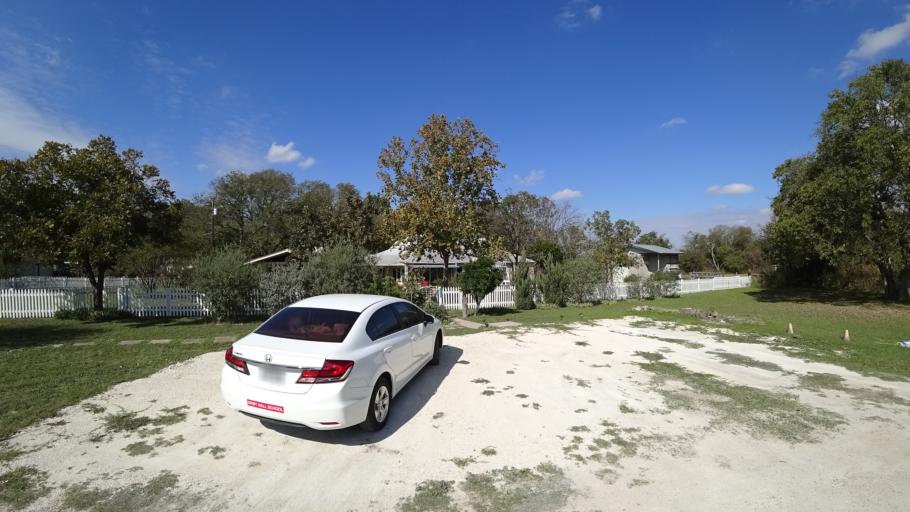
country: US
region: Texas
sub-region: Travis County
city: Windemere
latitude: 30.4533
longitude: -97.6404
